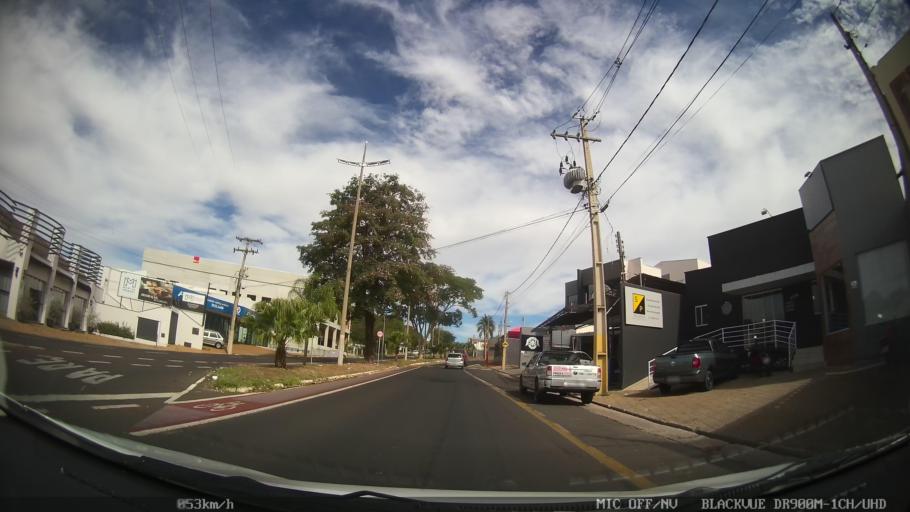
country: BR
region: Sao Paulo
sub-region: Catanduva
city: Catanduva
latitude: -21.1480
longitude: -48.9759
